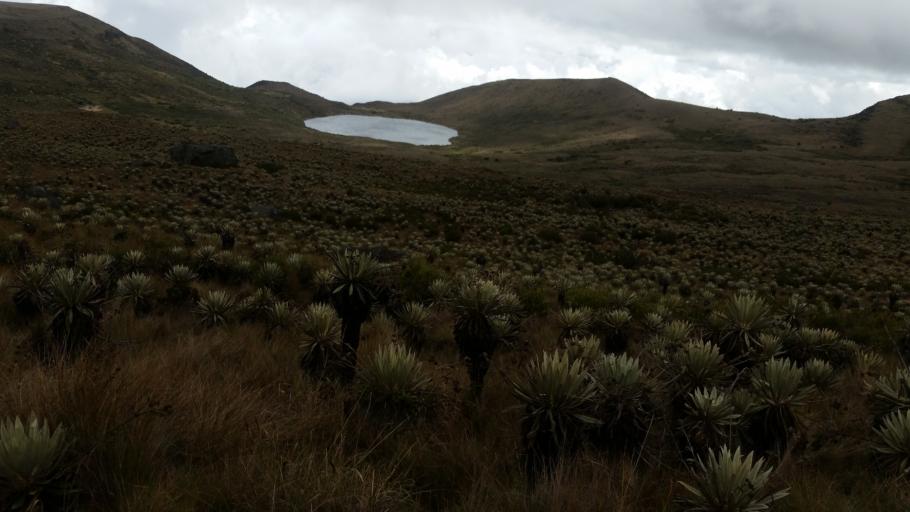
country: CO
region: Cundinamarca
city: Pasca
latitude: 4.3711
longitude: -74.2157
